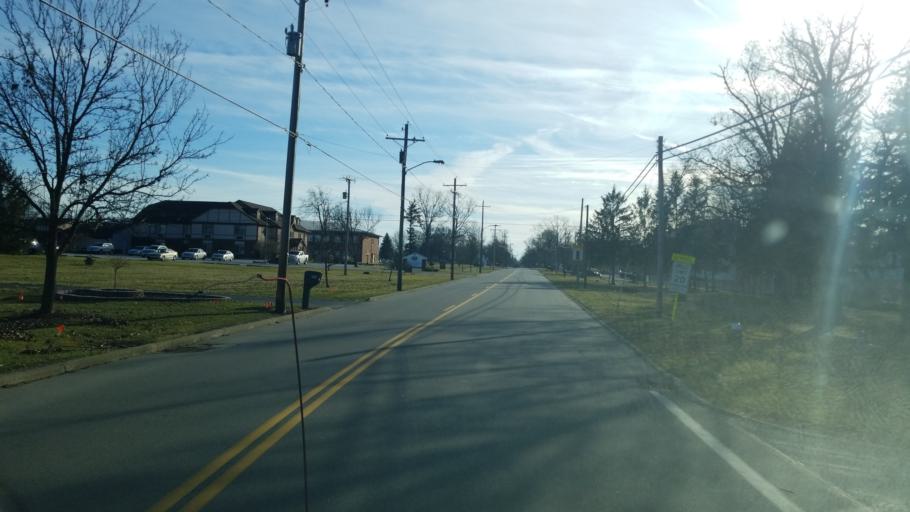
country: US
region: Ohio
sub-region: Sandusky County
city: Green Springs
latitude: 41.2645
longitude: -83.0519
